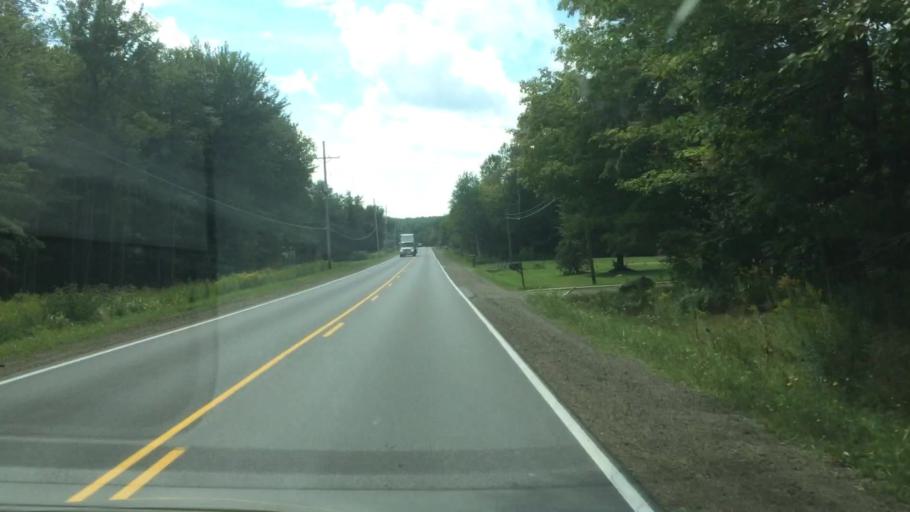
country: US
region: Pennsylvania
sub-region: McKean County
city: Bradford
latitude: 41.8752
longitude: -78.5830
